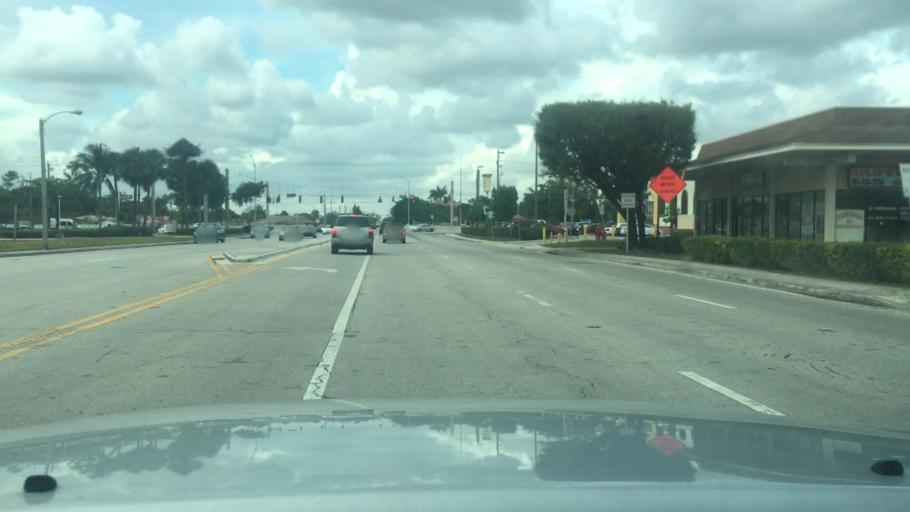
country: US
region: Florida
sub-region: Miami-Dade County
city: Tamiami
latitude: 25.7595
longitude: -80.3927
